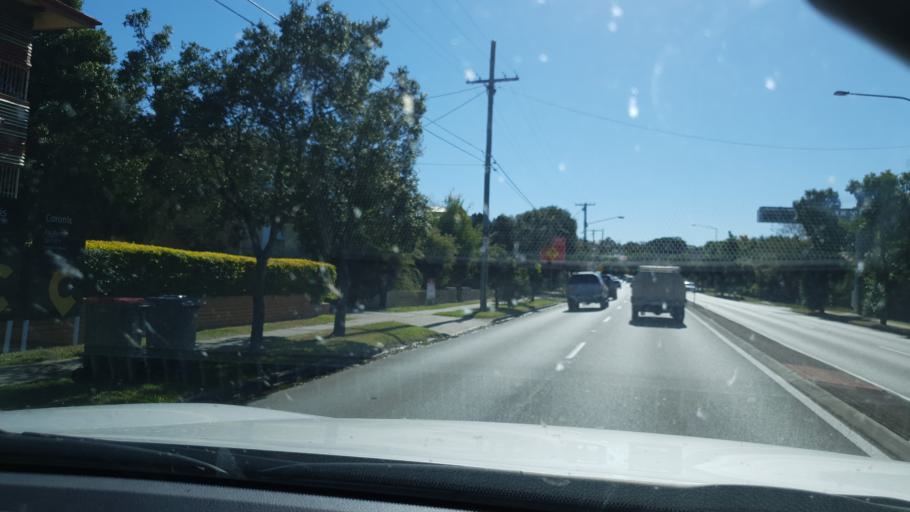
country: AU
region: Queensland
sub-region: Brisbane
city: Everton Park
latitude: -27.4043
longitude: 152.9885
